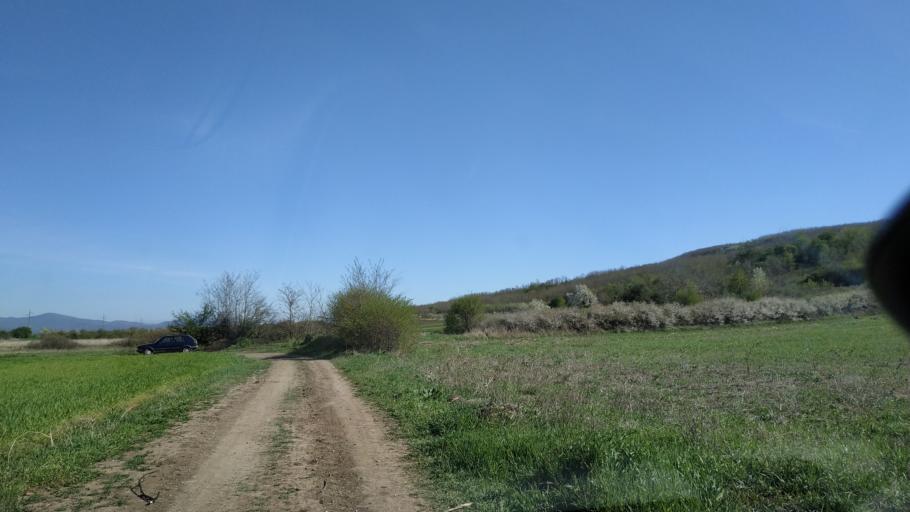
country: RS
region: Central Serbia
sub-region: Nisavski Okrug
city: Aleksinac
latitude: 43.4912
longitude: 21.6907
